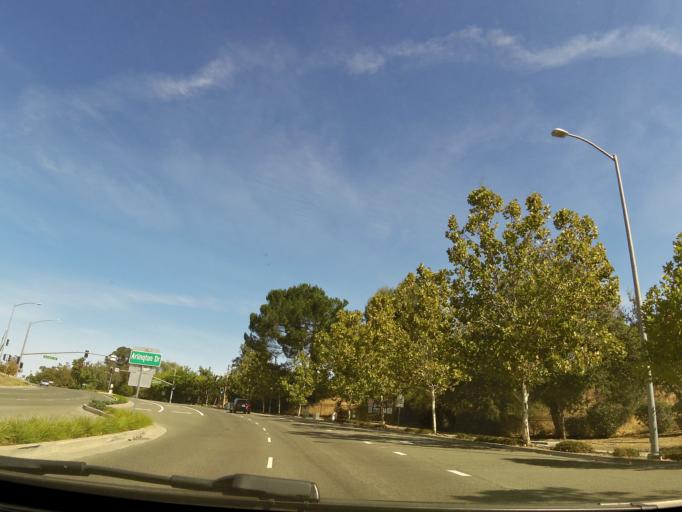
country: US
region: California
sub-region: Alameda County
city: Pleasanton
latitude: 37.6413
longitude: -121.8820
